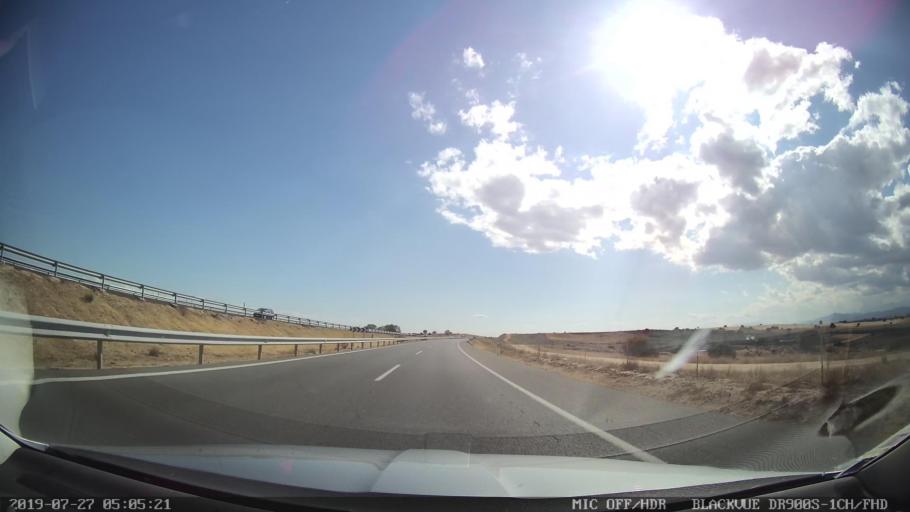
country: ES
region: Castille-La Mancha
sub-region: Province of Toledo
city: La Torre de Esteban Hambran
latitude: 40.1394
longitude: -4.1945
